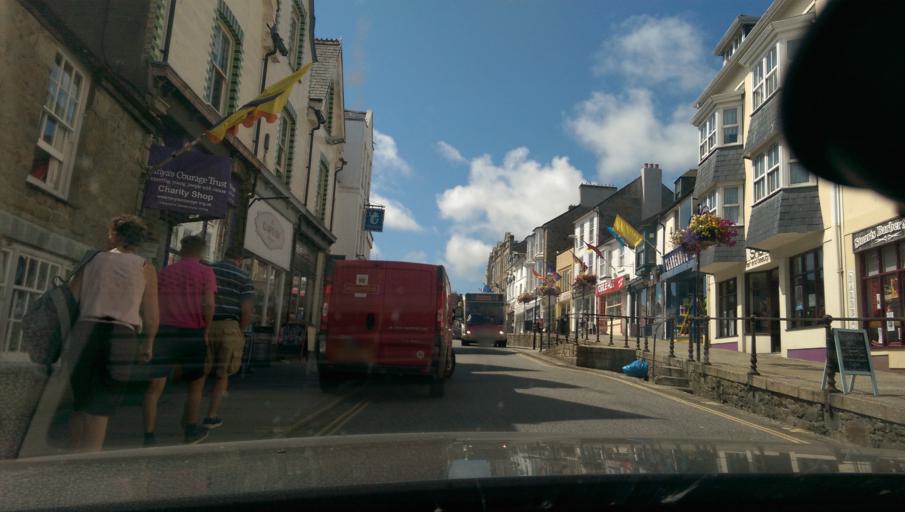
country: GB
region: England
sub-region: Cornwall
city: Penzance
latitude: 50.1207
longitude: -5.5343
